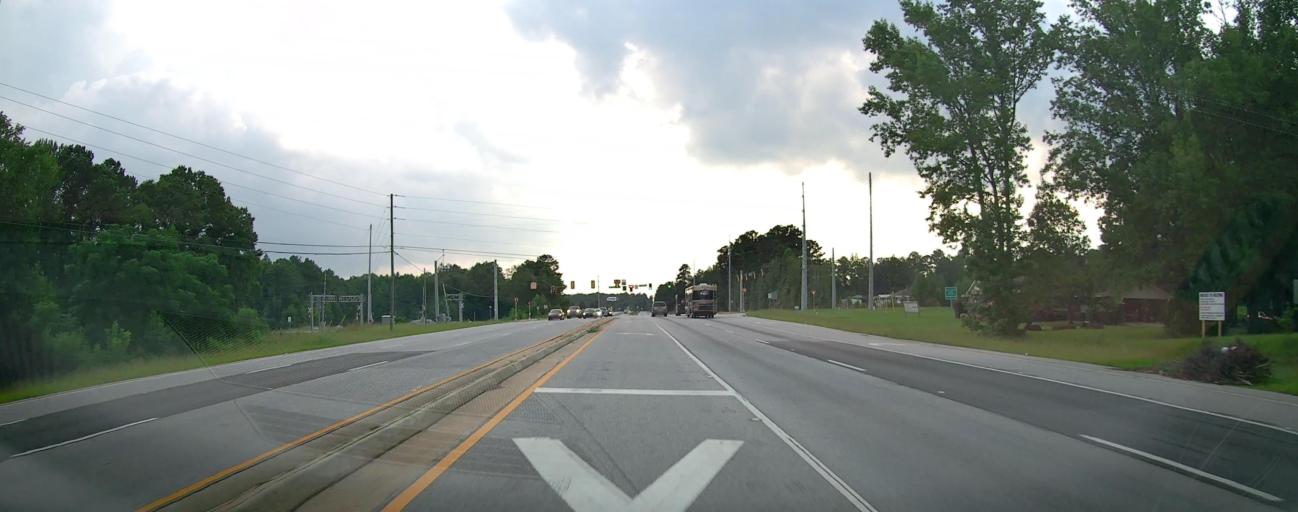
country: US
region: Georgia
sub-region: Muscogee County
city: Columbus
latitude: 32.5390
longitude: -84.8392
